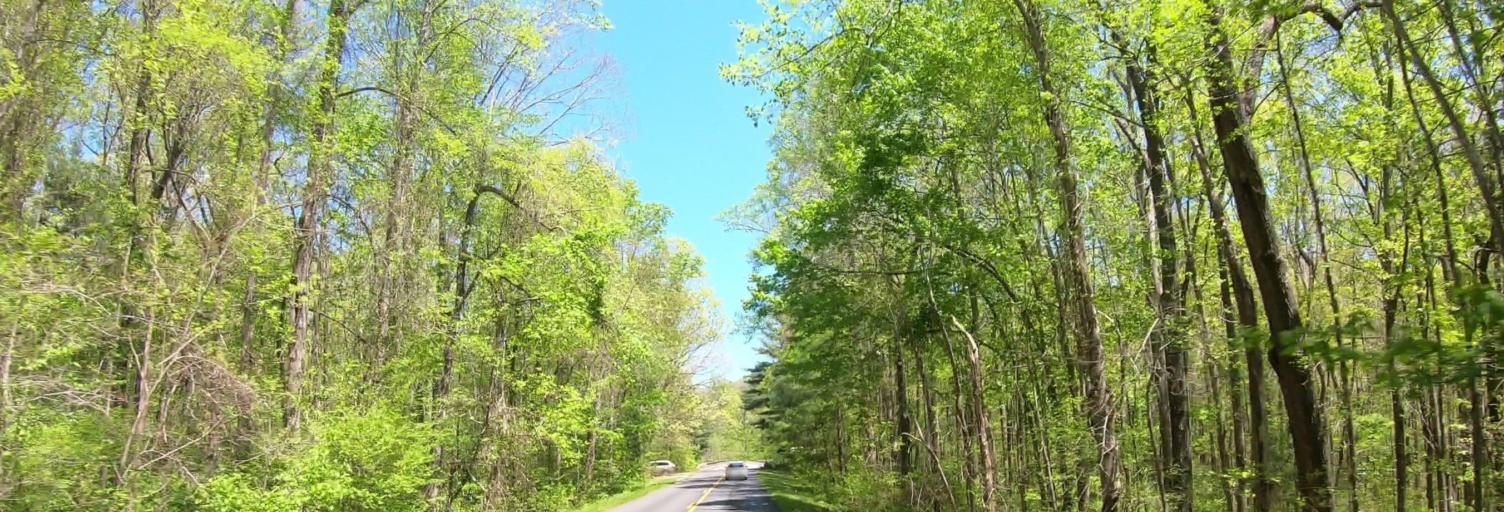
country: US
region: North Carolina
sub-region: Buncombe County
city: Biltmore Forest
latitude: 35.5244
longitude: -82.5213
